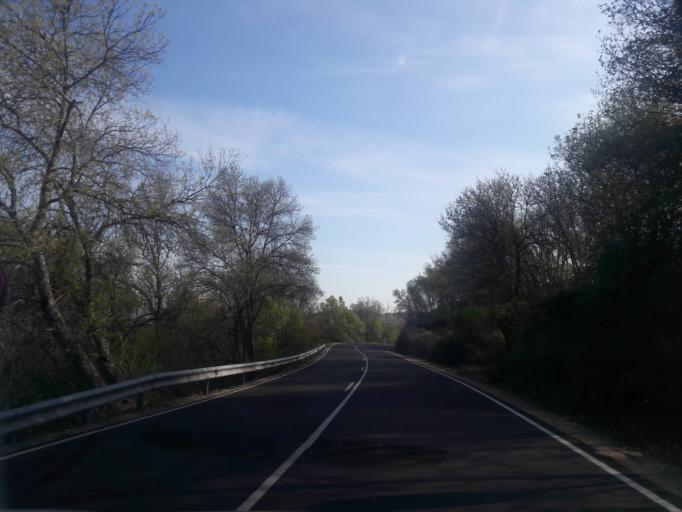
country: ES
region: Castille and Leon
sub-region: Provincia de Salamanca
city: Navalmoral de Bejar
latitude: 40.4110
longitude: -5.8066
